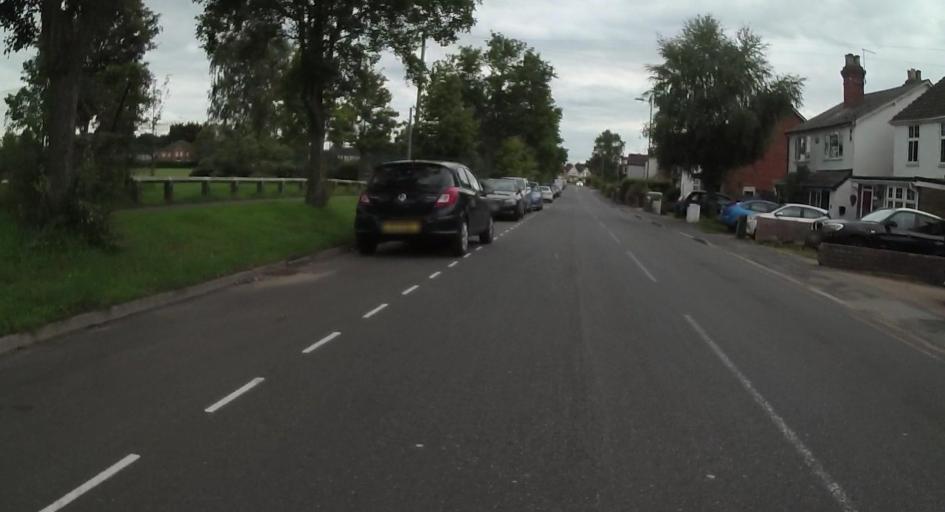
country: GB
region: England
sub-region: Hampshire
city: Farnborough
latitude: 51.2949
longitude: -0.7648
